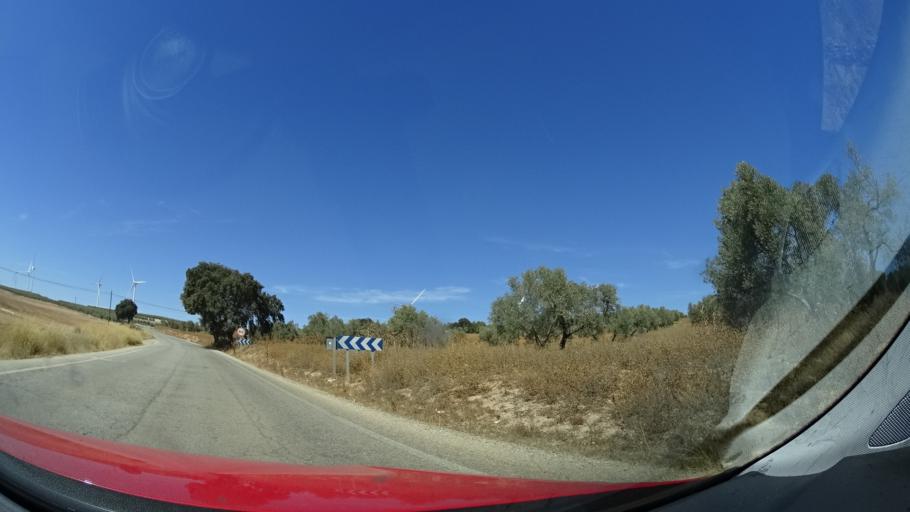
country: ES
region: Andalusia
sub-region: Provincia de Malaga
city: Sierra de Yeguas
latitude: 37.0994
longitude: -4.8682
